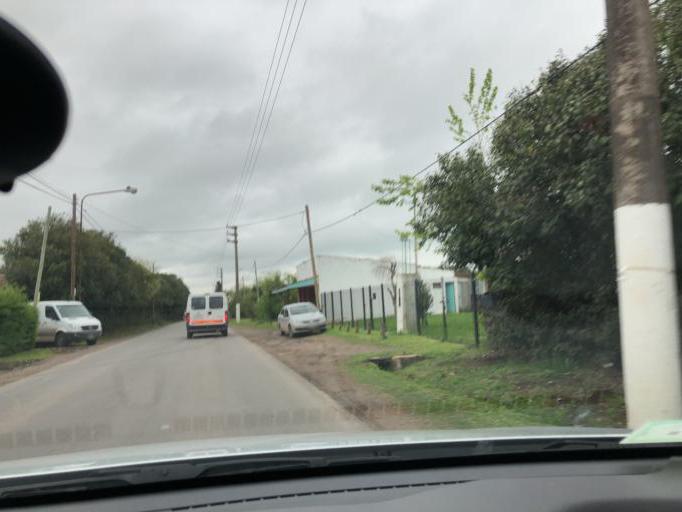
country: AR
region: Buenos Aires
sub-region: Partido de La Plata
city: La Plata
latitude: -34.9021
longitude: -58.0793
